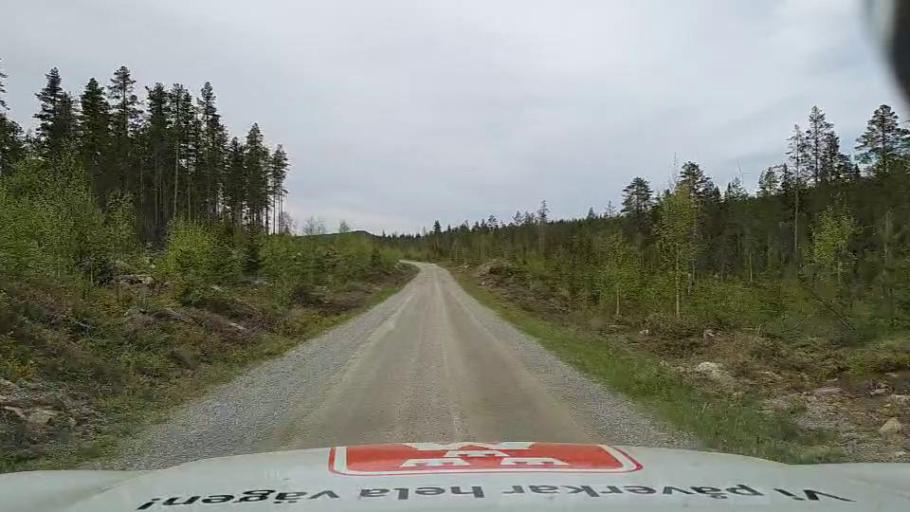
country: SE
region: Jaemtland
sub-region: Bergs Kommun
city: Hoverberg
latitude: 62.5485
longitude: 14.8979
